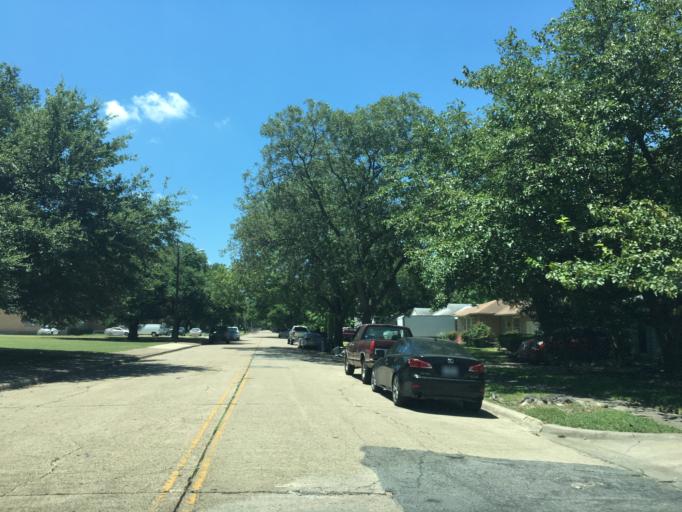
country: US
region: Texas
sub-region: Dallas County
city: Garland
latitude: 32.8474
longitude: -96.6757
